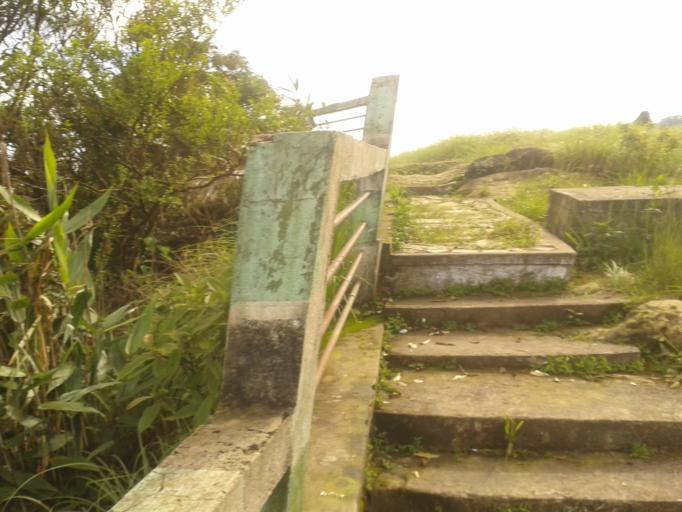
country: IN
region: Meghalaya
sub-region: East Khasi Hills
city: Cherrapunji
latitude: 25.2452
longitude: 91.7412
